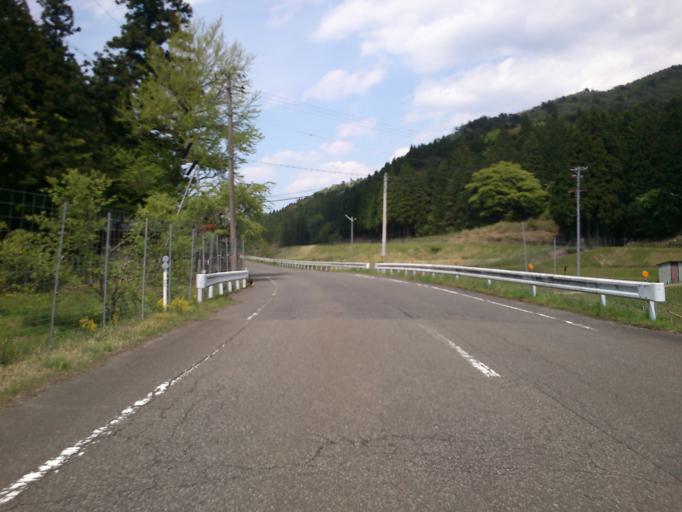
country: JP
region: Kyoto
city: Fukuchiyama
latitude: 35.3806
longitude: 134.9393
